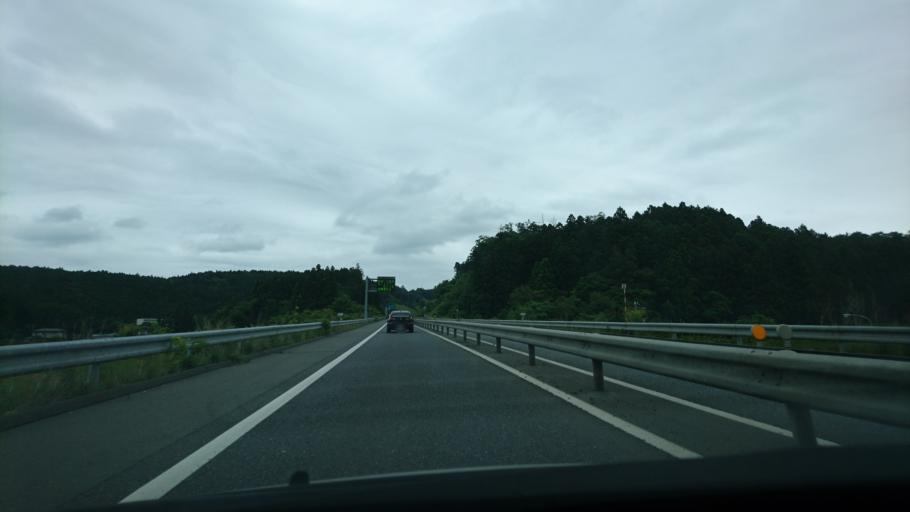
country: JP
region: Miyagi
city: Wakuya
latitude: 38.7034
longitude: 141.2981
